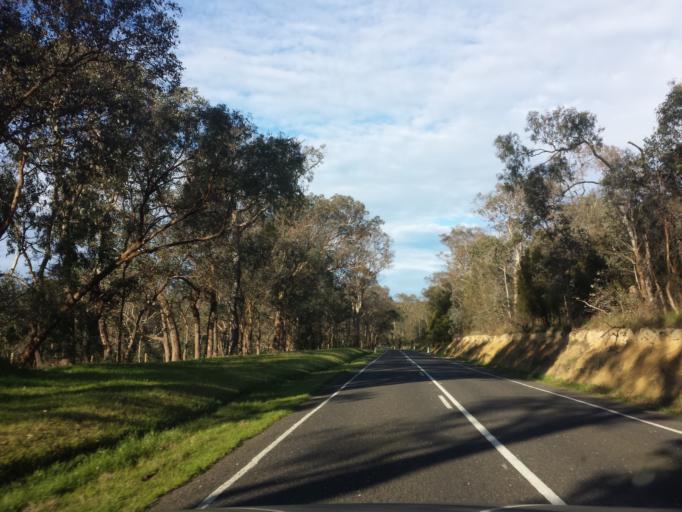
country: AU
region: Victoria
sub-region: Yarra Ranges
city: Yarra Glen
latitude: -37.6491
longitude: 145.3253
